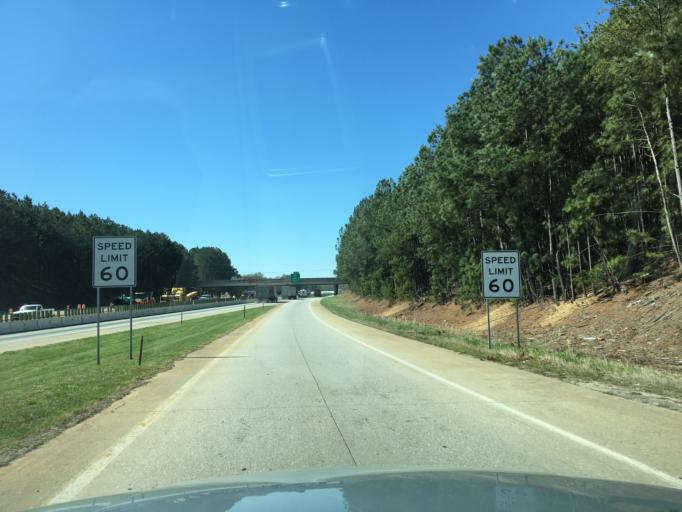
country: US
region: South Carolina
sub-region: Spartanburg County
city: Southern Shops
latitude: 34.9960
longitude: -81.9945
